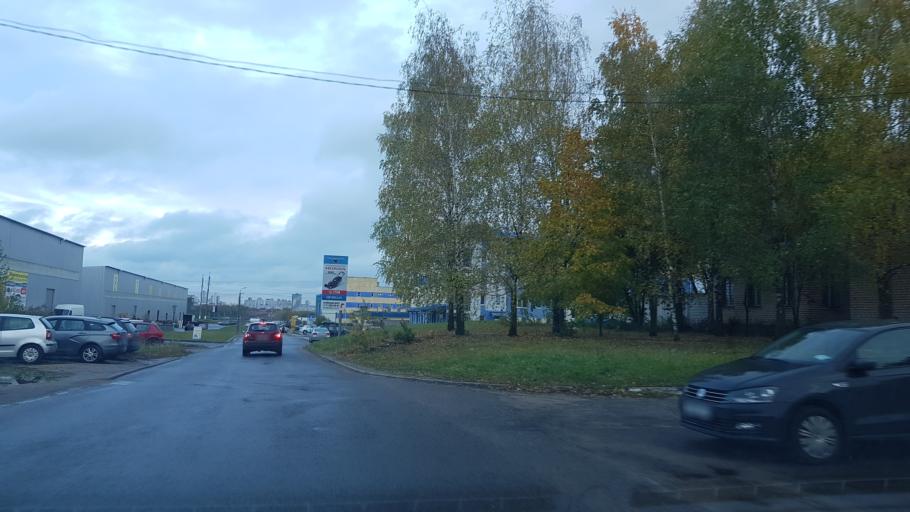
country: BY
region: Minsk
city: Malinovka
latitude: 53.8765
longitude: 27.4115
